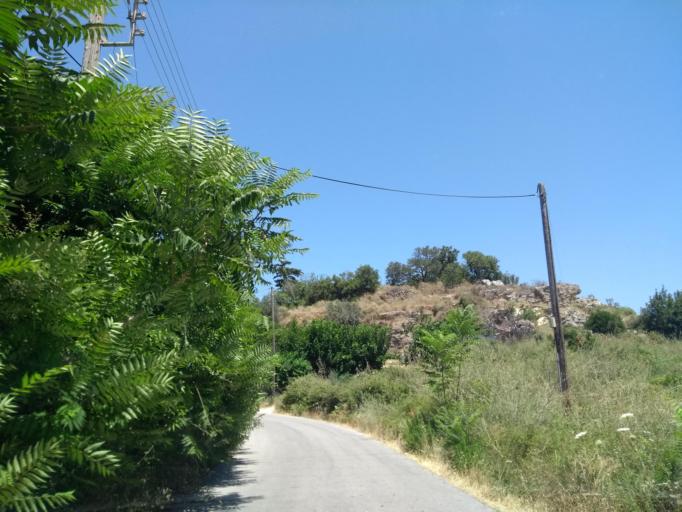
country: GR
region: Crete
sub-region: Nomos Chanias
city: Georgioupolis
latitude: 35.3146
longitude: 24.3003
